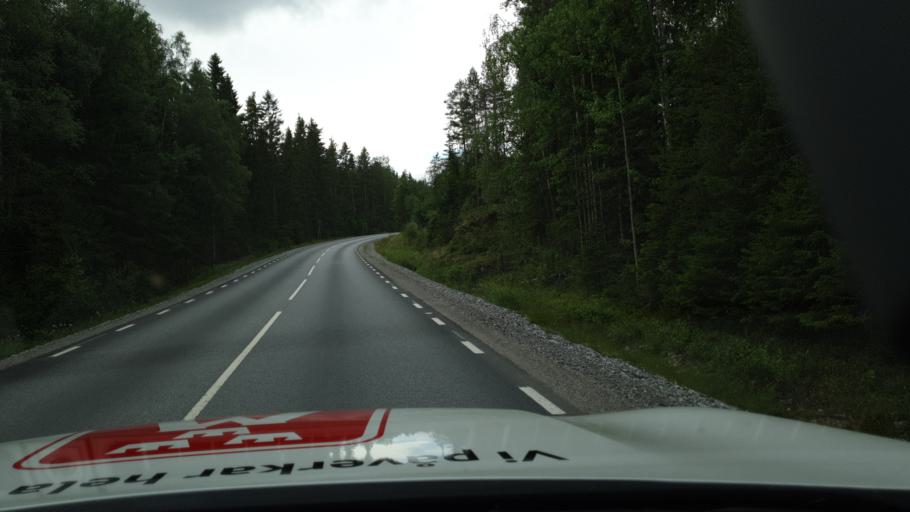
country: SE
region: Vaesterbotten
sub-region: Nordmalings Kommun
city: Nordmaling
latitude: 63.5707
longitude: 19.4256
